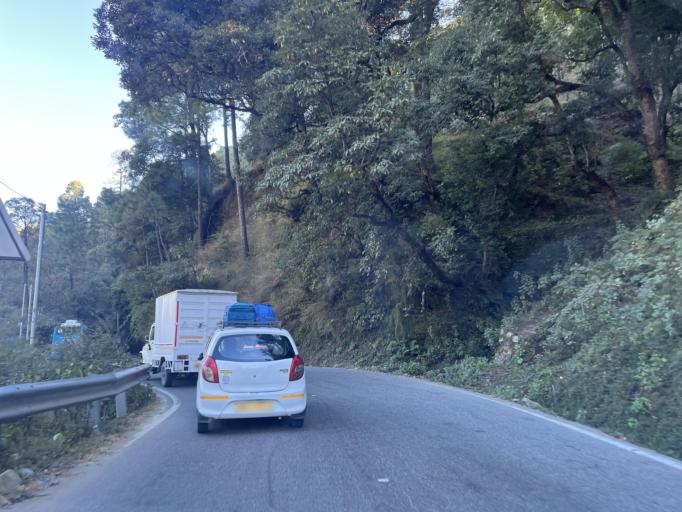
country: IN
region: Uttarakhand
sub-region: Naini Tal
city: Bhowali
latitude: 29.3948
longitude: 79.5113
